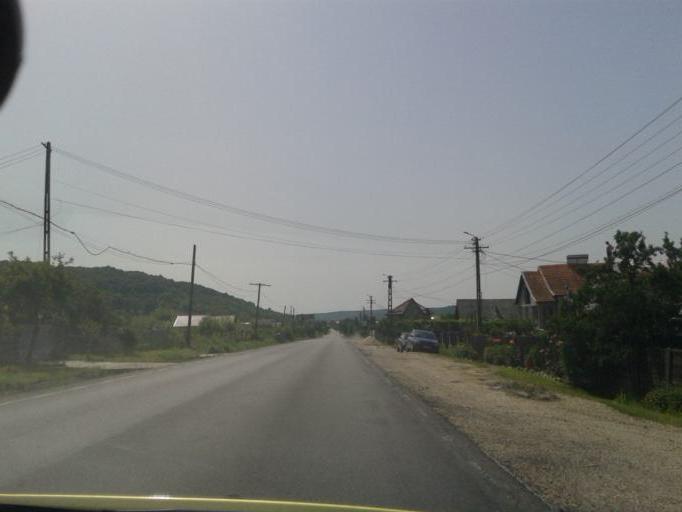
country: RO
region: Arges
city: Draganu-Olteni
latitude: 44.9124
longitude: 24.7220
